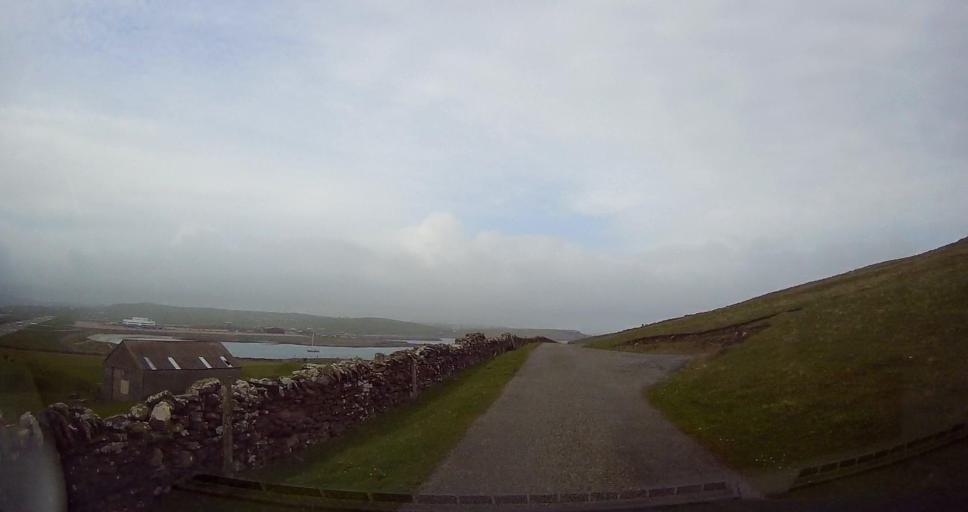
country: GB
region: Scotland
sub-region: Shetland Islands
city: Sandwick
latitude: 59.8688
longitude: -1.2793
